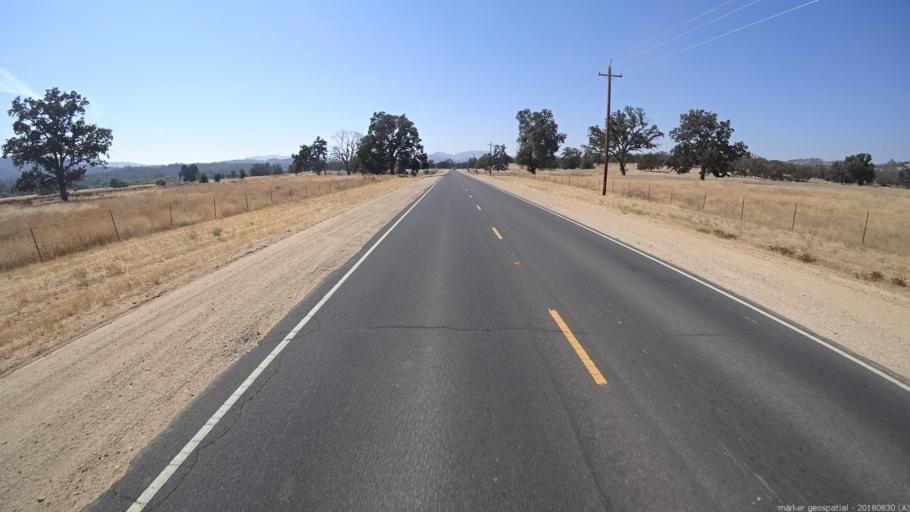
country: US
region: California
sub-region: Monterey County
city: King City
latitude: 35.9721
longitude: -121.2026
